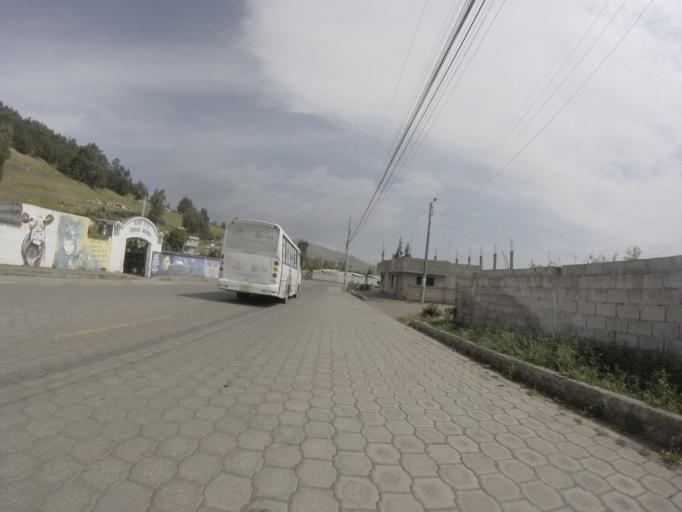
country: EC
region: Pichincha
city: Cayambe
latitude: 0.1493
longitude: -78.0709
